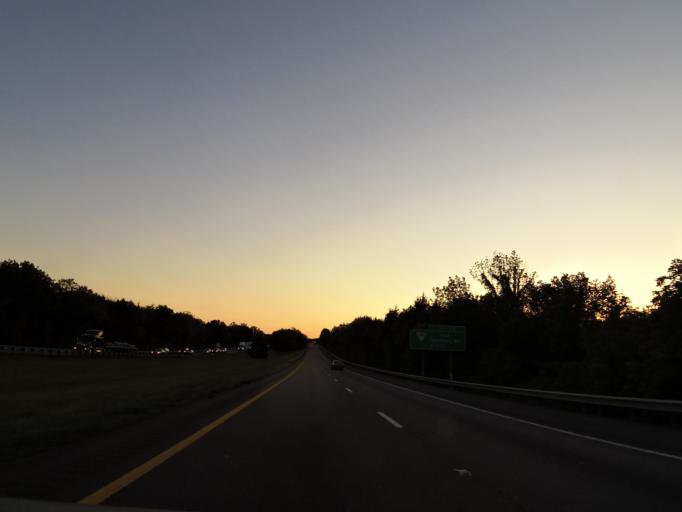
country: US
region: Tennessee
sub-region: Hamblen County
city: Morristown
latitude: 36.1974
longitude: -83.1531
